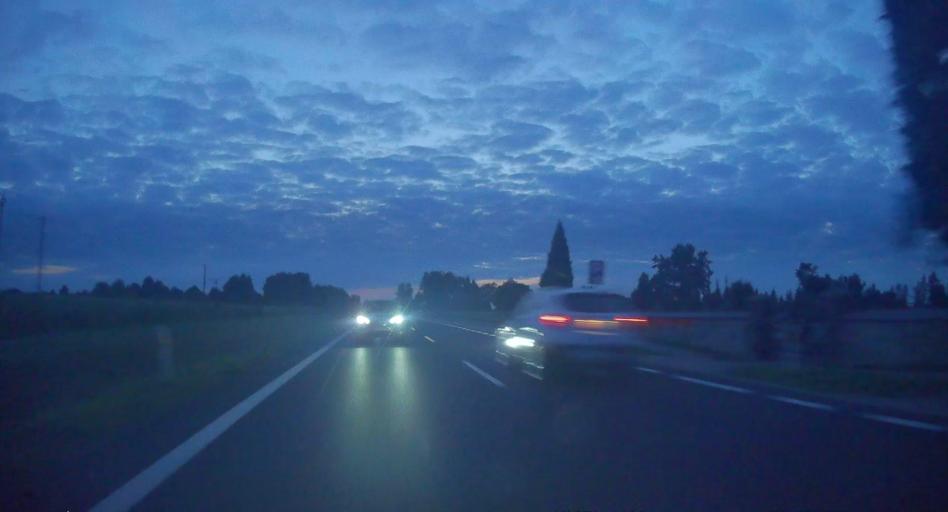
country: PL
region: Silesian Voivodeship
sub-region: Powiat klobucki
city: Klobuck
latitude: 50.8952
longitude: 18.9533
